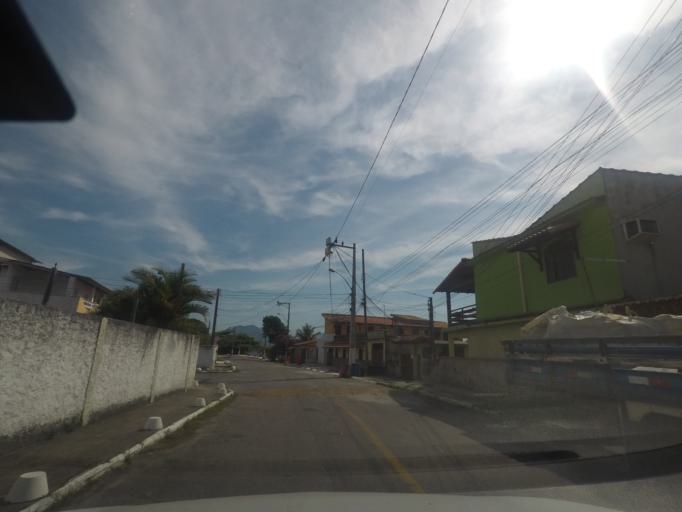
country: BR
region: Rio de Janeiro
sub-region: Marica
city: Marica
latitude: -22.9557
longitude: -42.8101
